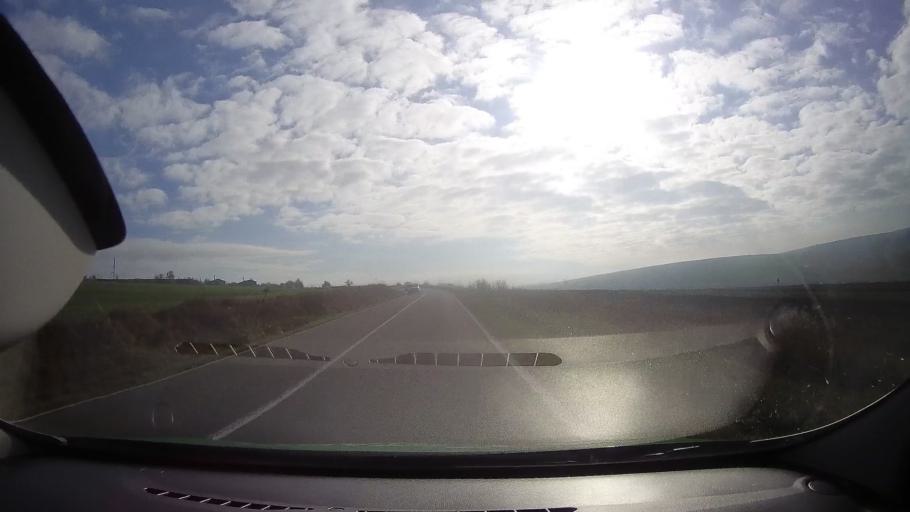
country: RO
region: Tulcea
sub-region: Comuna Bestepe
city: Bestepe
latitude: 45.0829
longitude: 29.0233
